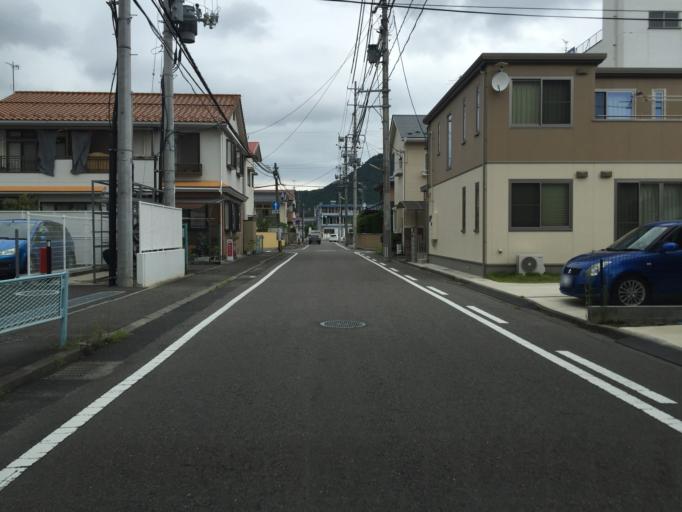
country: JP
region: Fukushima
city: Fukushima-shi
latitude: 37.7584
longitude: 140.4549
